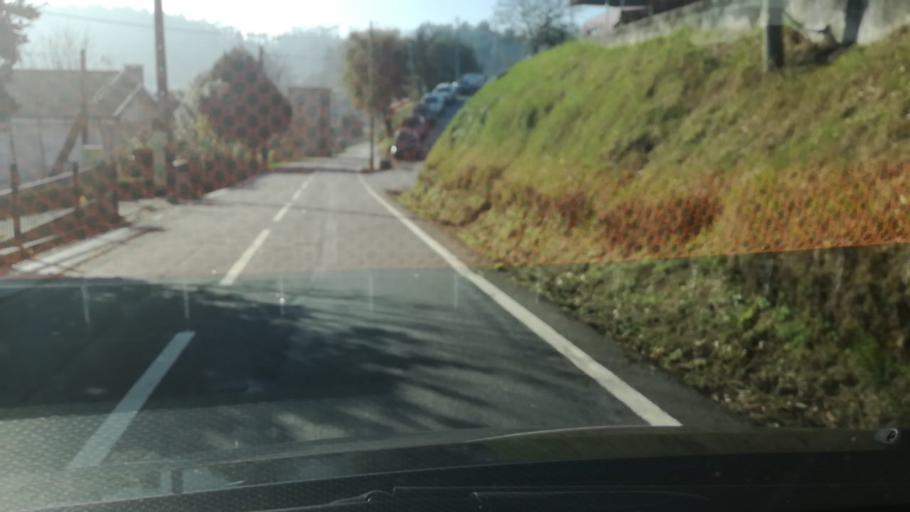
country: PT
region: Braga
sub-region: Guimaraes
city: Ponte
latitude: 41.5262
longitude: -8.3408
